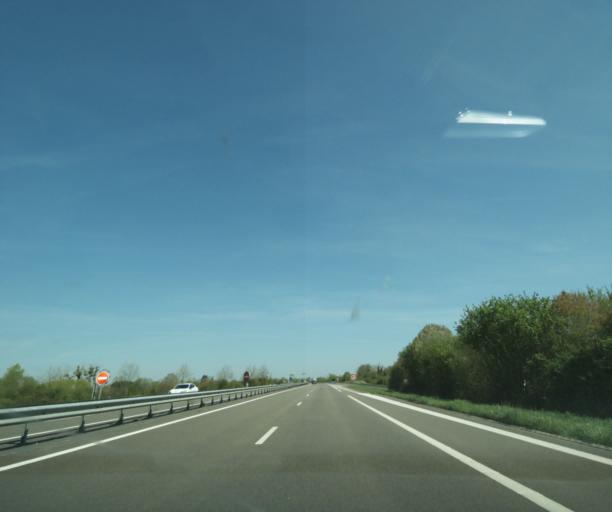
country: FR
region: Bourgogne
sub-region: Departement de la Nievre
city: Saint-Eloi
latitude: 46.9792
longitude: 3.2018
